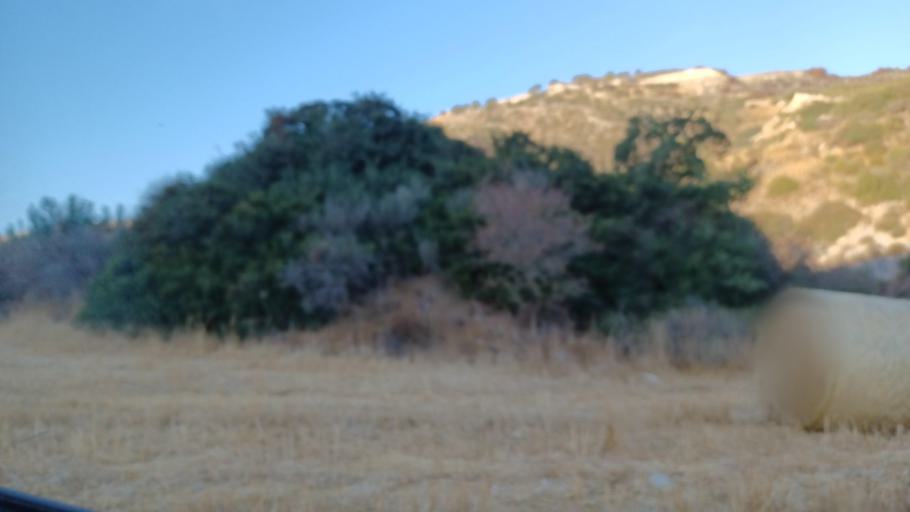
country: CY
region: Pafos
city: Polis
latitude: 34.9986
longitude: 32.4267
